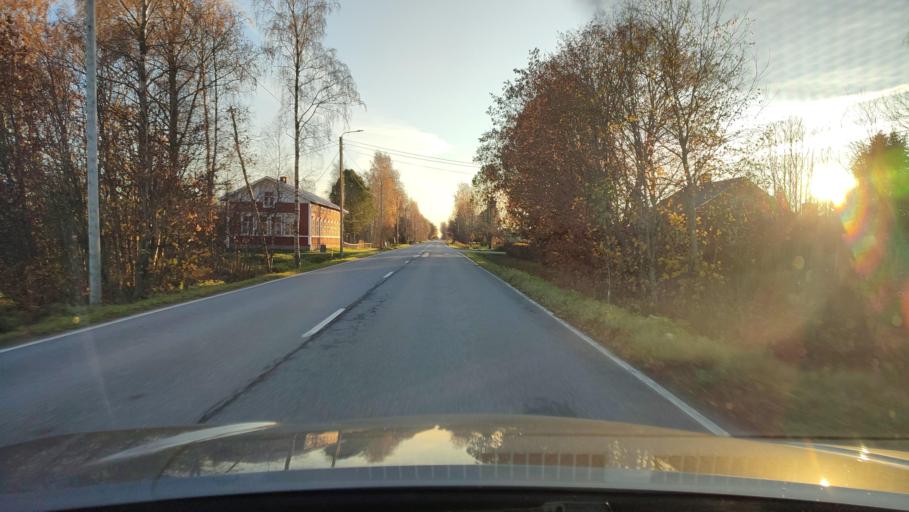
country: FI
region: Ostrobothnia
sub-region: Sydosterbotten
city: Naerpes
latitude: 62.5970
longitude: 21.4511
